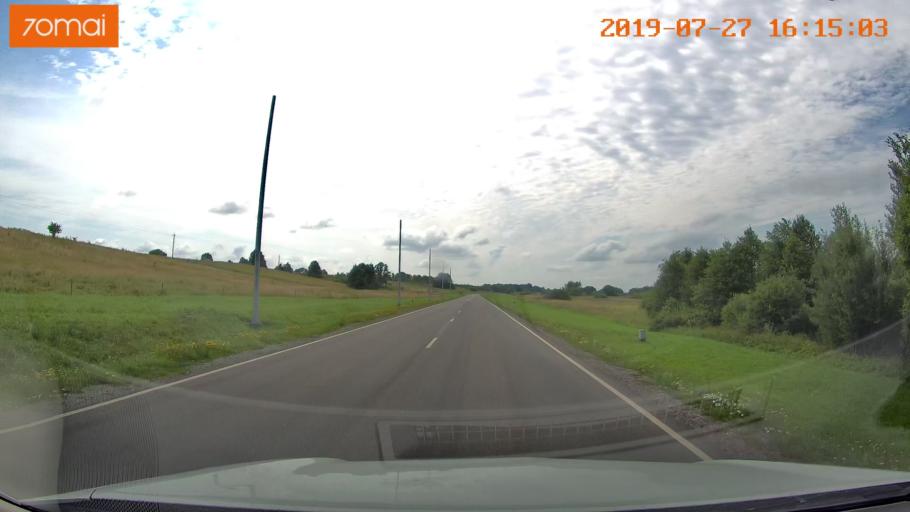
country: RU
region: Kaliningrad
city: Chernyakhovsk
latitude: 54.6254
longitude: 21.6066
